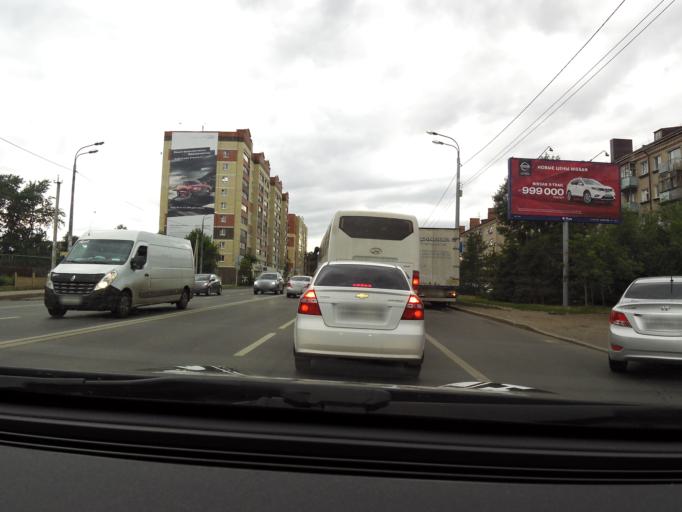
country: RU
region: Tatarstan
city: Staroye Arakchino
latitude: 55.8251
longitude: 49.0399
